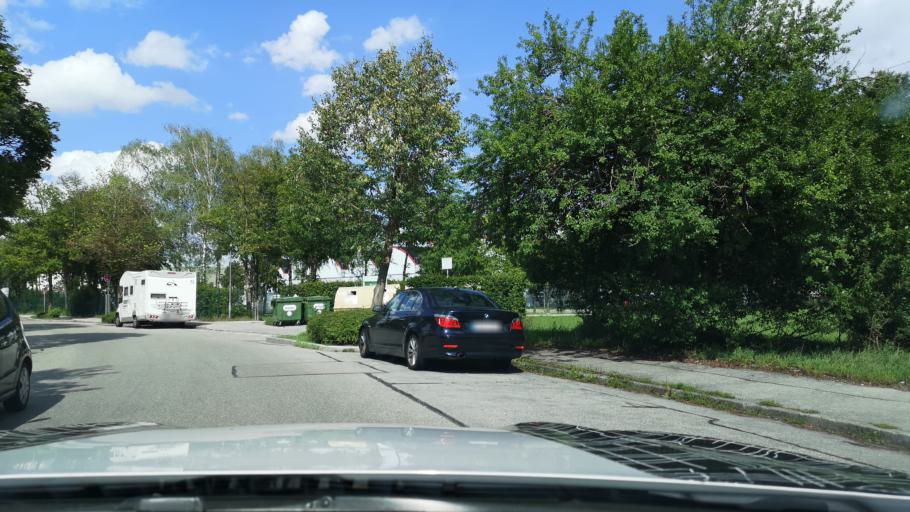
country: DE
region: Bavaria
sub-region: Upper Bavaria
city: Garching bei Munchen
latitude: 48.2478
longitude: 11.6126
